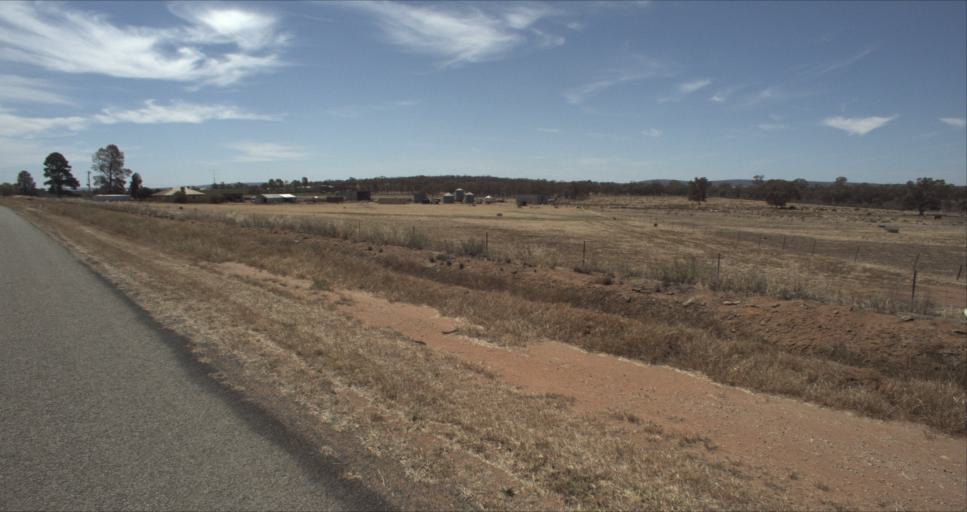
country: AU
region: New South Wales
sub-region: Leeton
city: Leeton
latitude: -34.5993
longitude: 146.4790
